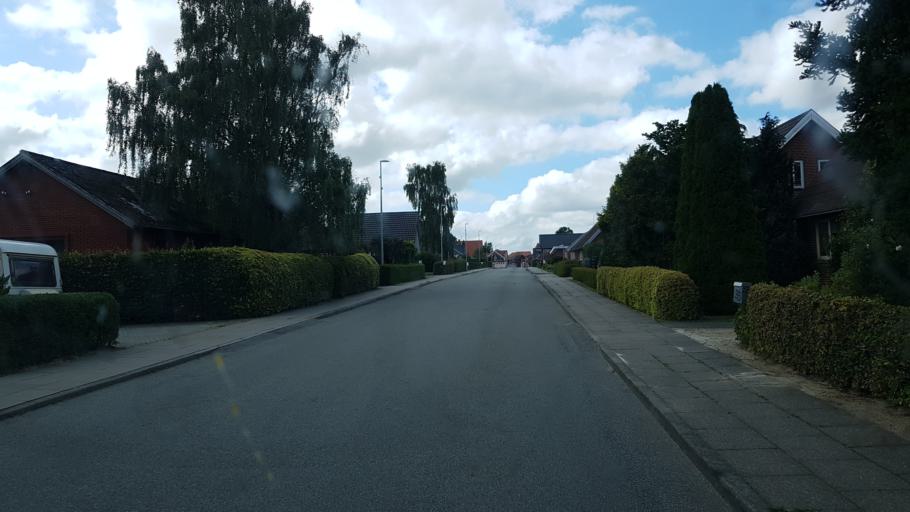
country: DK
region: South Denmark
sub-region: Billund Kommune
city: Grindsted
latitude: 55.7033
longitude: 8.7592
